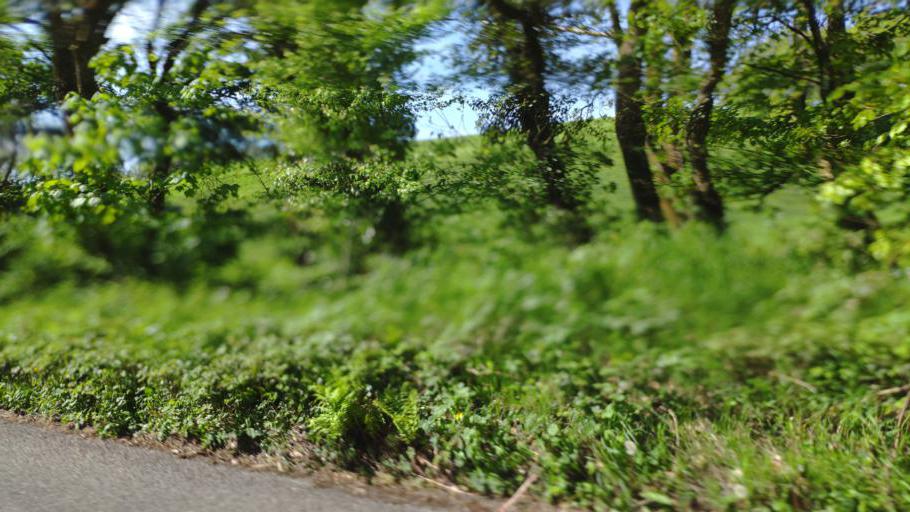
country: IE
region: Munster
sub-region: County Cork
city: Blarney
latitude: 51.9685
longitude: -8.5780
